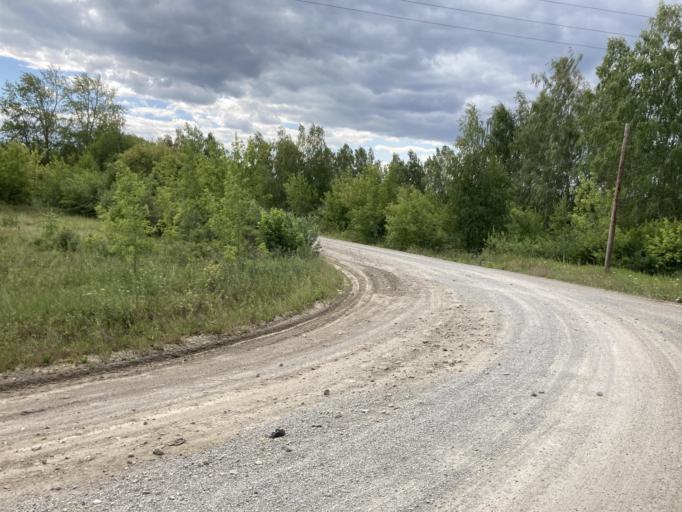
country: RU
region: Sverdlovsk
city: Bogdanovich
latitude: 56.7925
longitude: 62.0615
